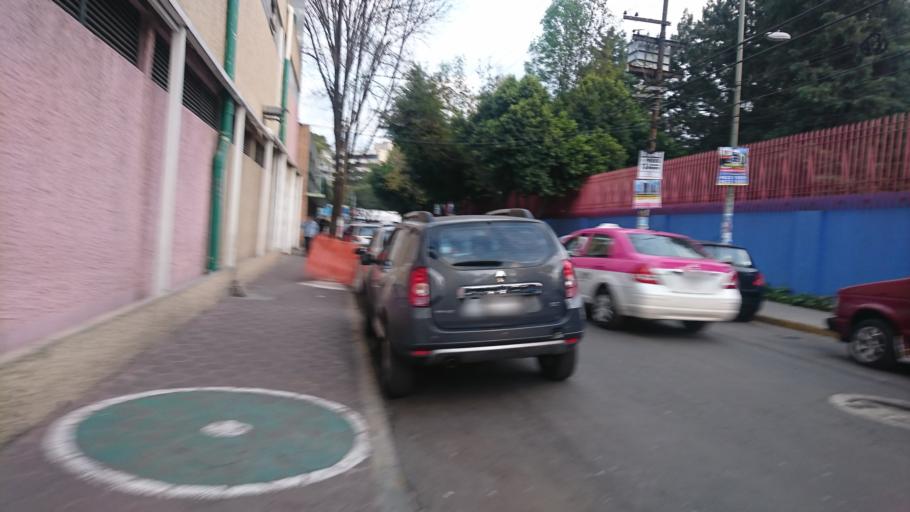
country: MX
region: Mexico City
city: Coyoacan
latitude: 19.3597
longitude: -99.1643
